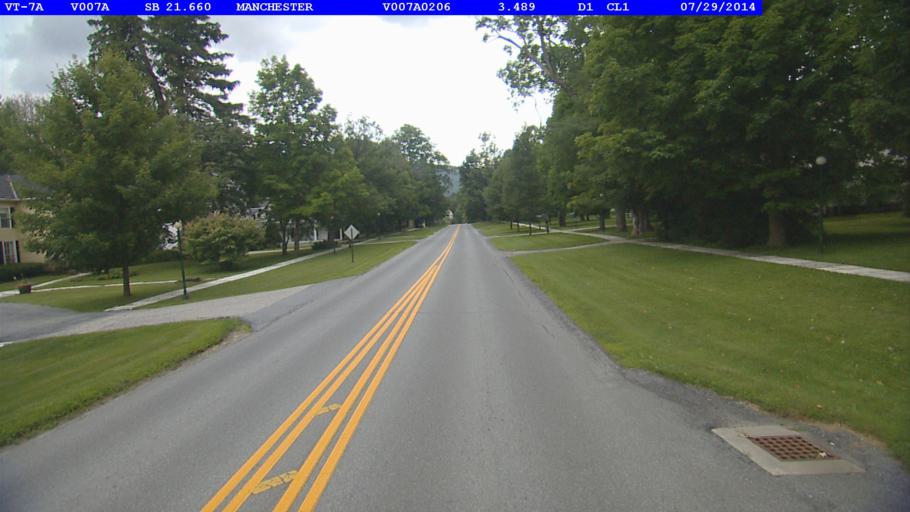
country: US
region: Vermont
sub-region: Bennington County
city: Manchester Center
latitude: 43.1609
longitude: -73.0722
